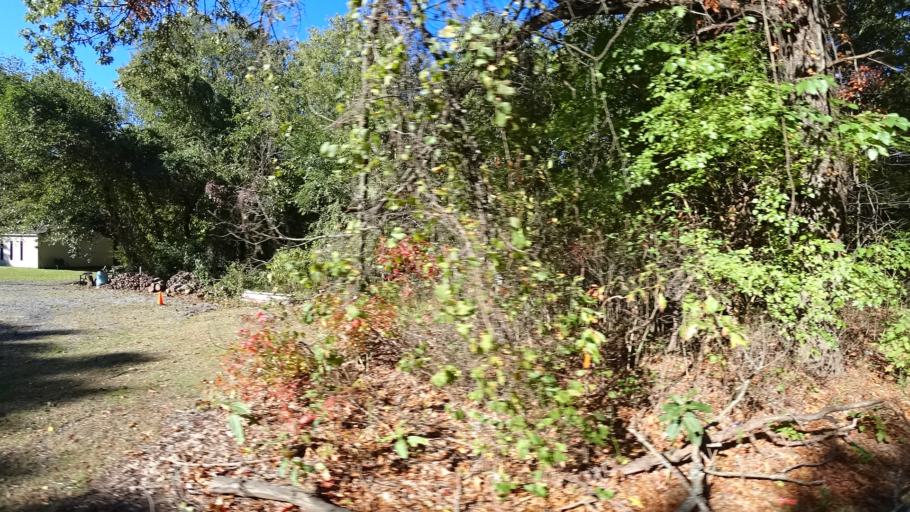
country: US
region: Indiana
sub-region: LaPorte County
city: Michigan City
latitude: 41.6931
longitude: -86.9325
